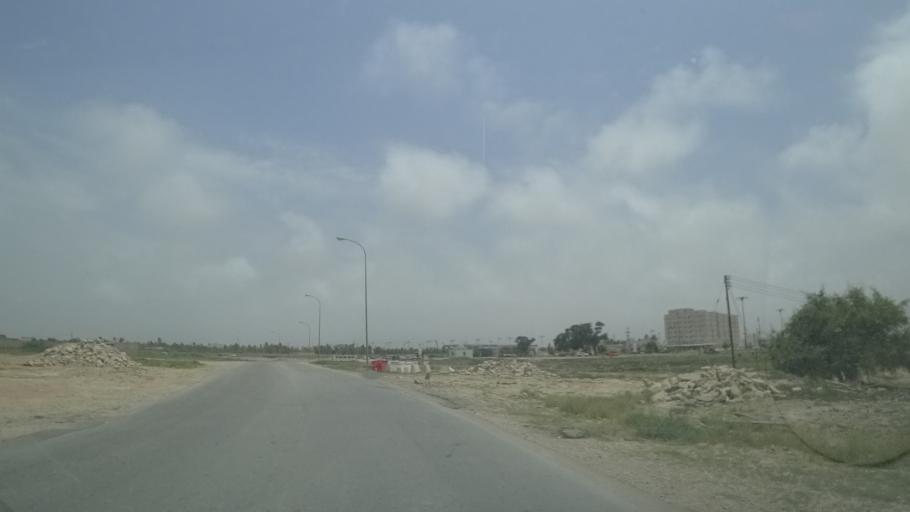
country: OM
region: Zufar
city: Salalah
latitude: 17.0236
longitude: 54.1735
